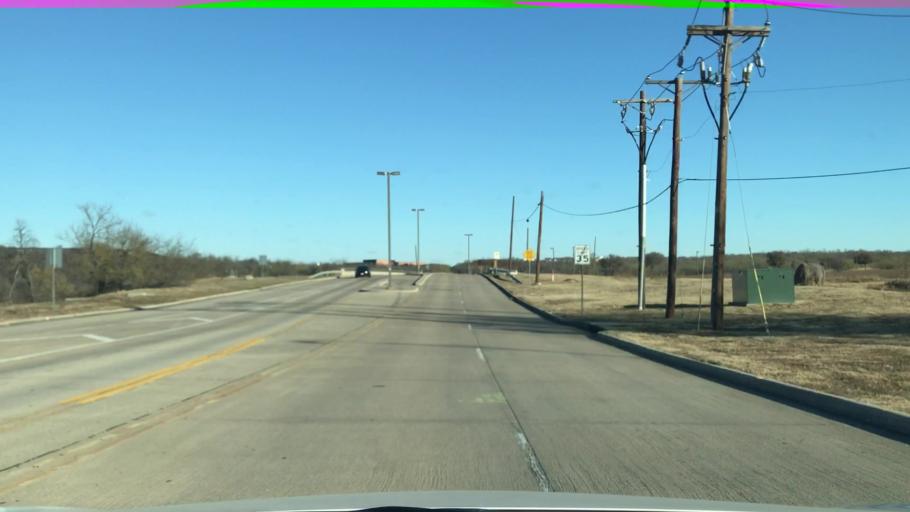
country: US
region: Texas
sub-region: Dallas County
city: Farmers Branch
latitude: 32.8829
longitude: -96.9468
